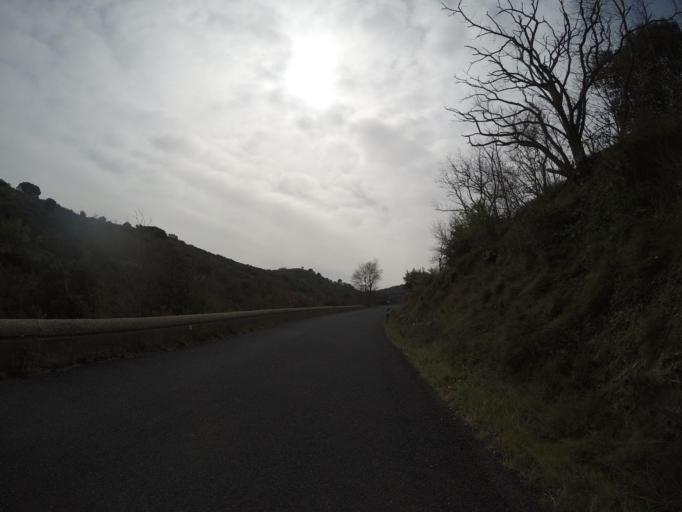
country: FR
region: Languedoc-Roussillon
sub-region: Departement des Pyrenees-Orientales
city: Estagel
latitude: 42.7476
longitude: 2.7245
